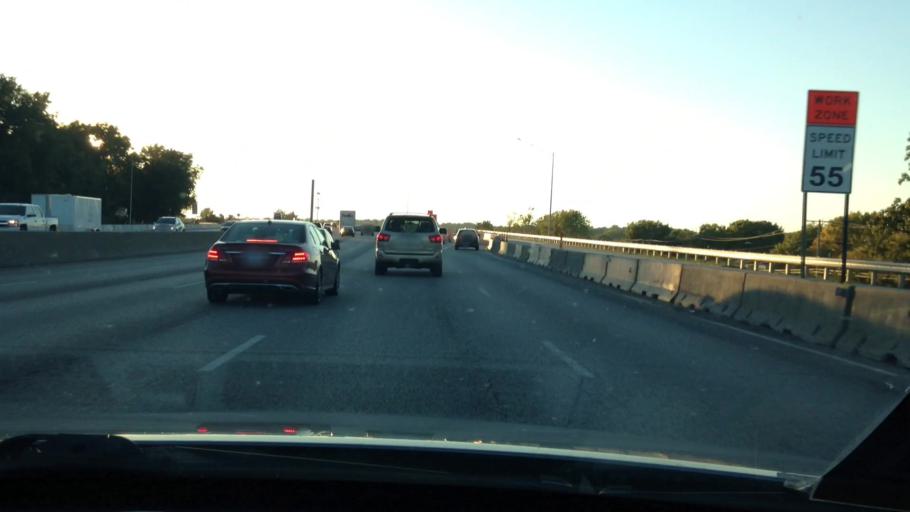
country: US
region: Kansas
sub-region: Johnson County
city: Leawood
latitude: 38.9402
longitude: -94.5914
